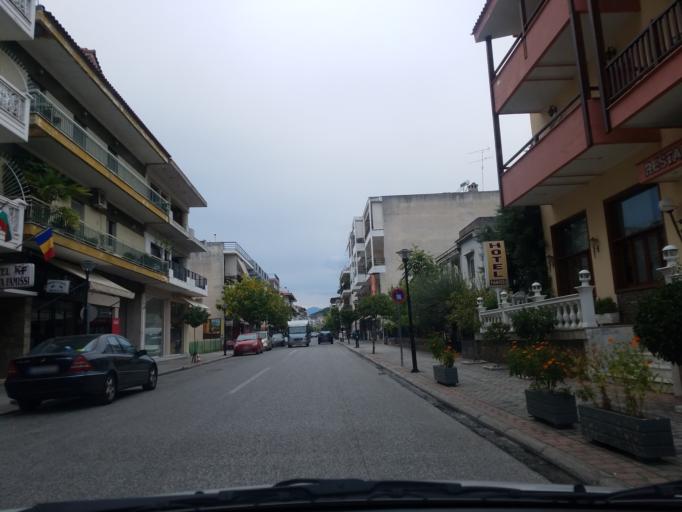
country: GR
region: Thessaly
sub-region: Trikala
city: Kalampaka
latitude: 39.7028
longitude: 21.6316
